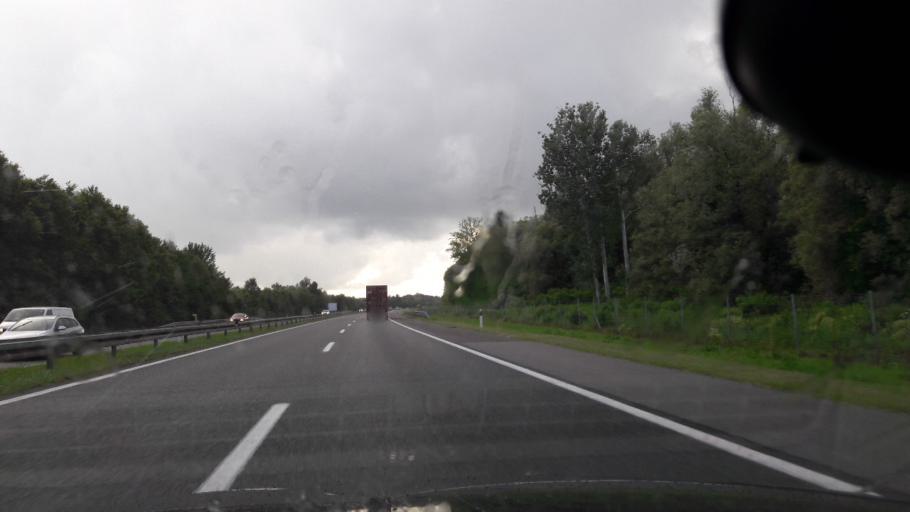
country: HR
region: Sisacko-Moslavacka
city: Novska
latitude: 45.3105
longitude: 16.9965
